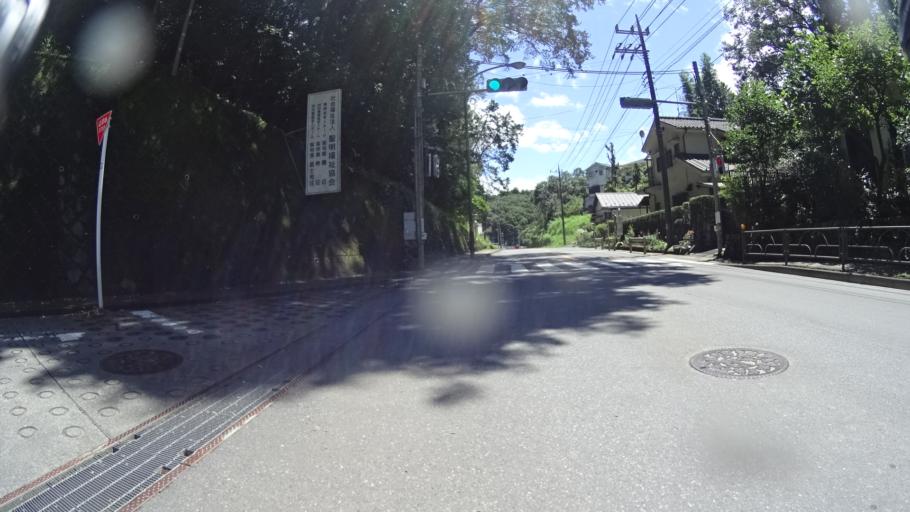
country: JP
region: Tokyo
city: Ome
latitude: 35.8056
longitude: 139.2650
